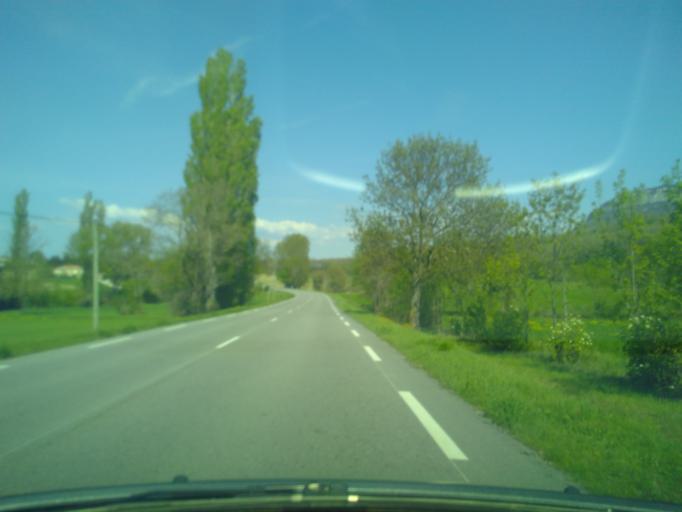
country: FR
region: Rhone-Alpes
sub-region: Departement de la Drome
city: Crest
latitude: 44.6625
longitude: 4.9965
